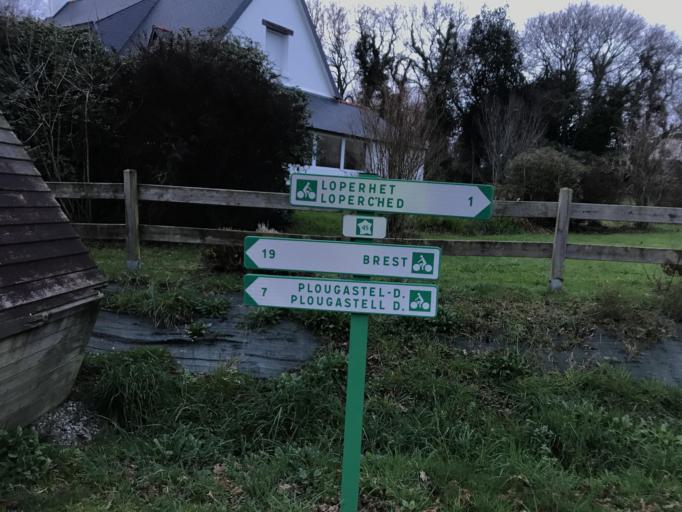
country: FR
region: Brittany
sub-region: Departement du Finistere
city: Loperhet
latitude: 48.3716
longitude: -4.3180
